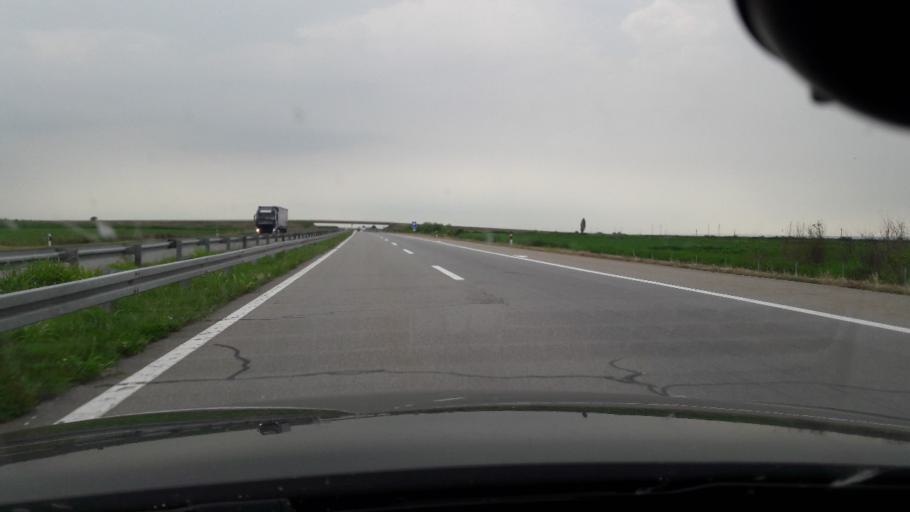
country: RS
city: Macvanska Mitrovica
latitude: 45.0171
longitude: 19.5522
